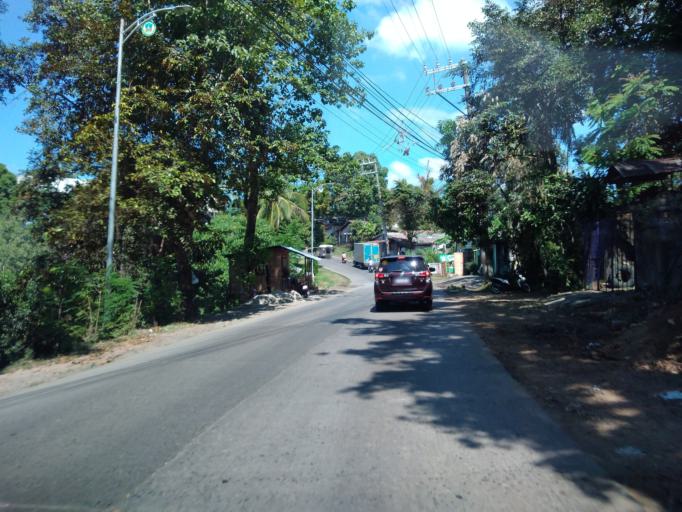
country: PH
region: Central Luzon
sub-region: Province of Bulacan
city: Bitungol
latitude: 14.8600
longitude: 121.0701
